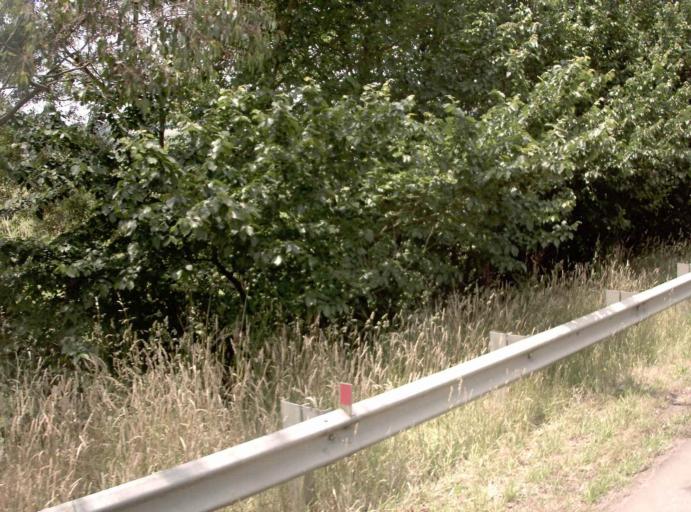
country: AU
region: Victoria
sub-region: Latrobe
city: Traralgon
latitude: -38.2879
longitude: 146.6995
